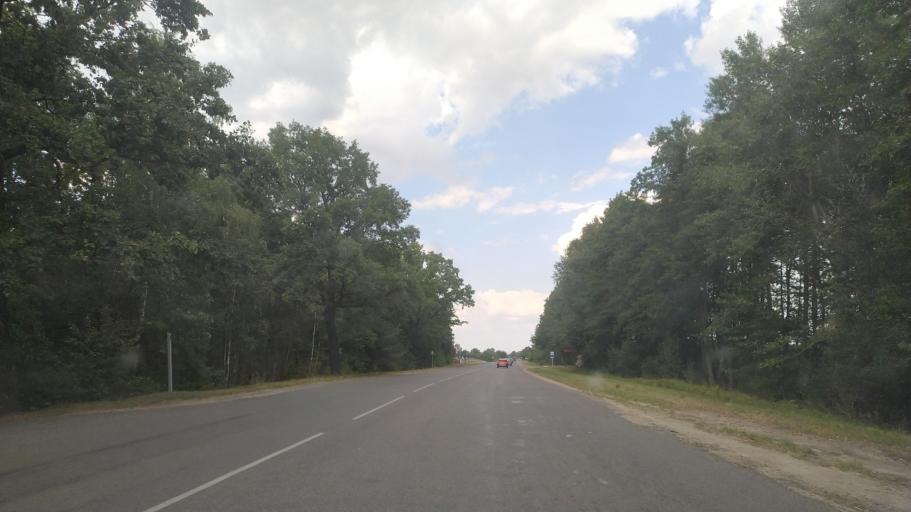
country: BY
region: Brest
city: Drahichyn
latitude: 52.1075
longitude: 25.1146
